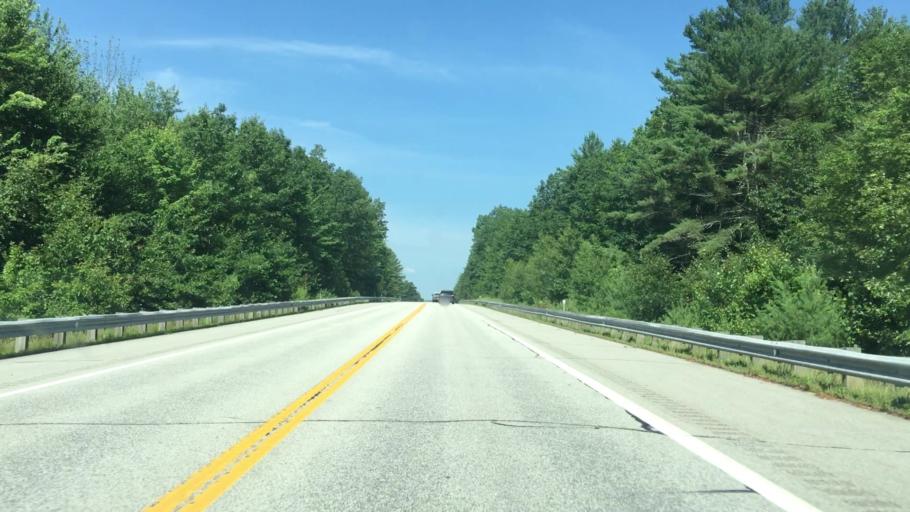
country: US
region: New Hampshire
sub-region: Merrimack County
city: Henniker
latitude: 43.1814
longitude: -71.7678
